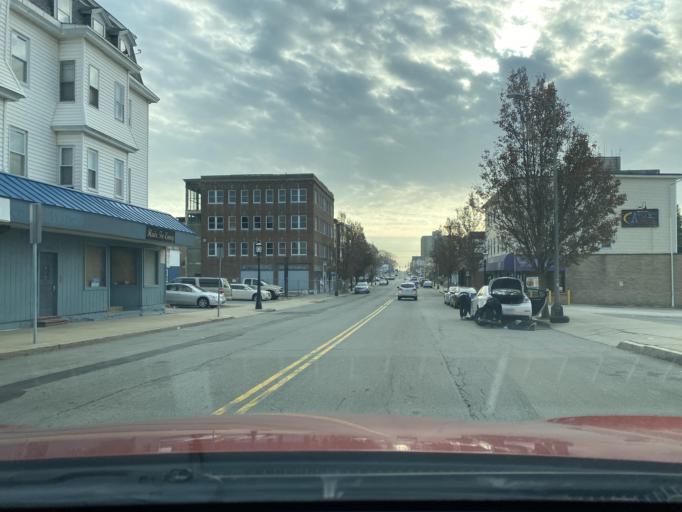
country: US
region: Massachusetts
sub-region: Bristol County
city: Fall River
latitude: 41.6890
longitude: -71.1323
